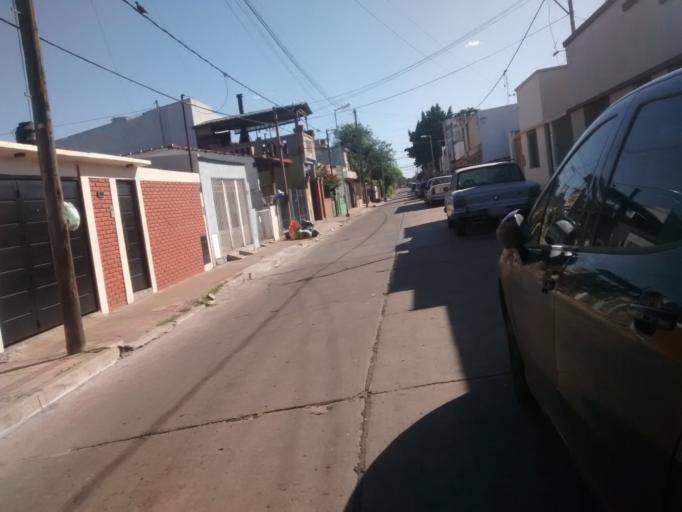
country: AR
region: Buenos Aires
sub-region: Partido de La Plata
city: La Plata
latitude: -34.9303
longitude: -57.9200
